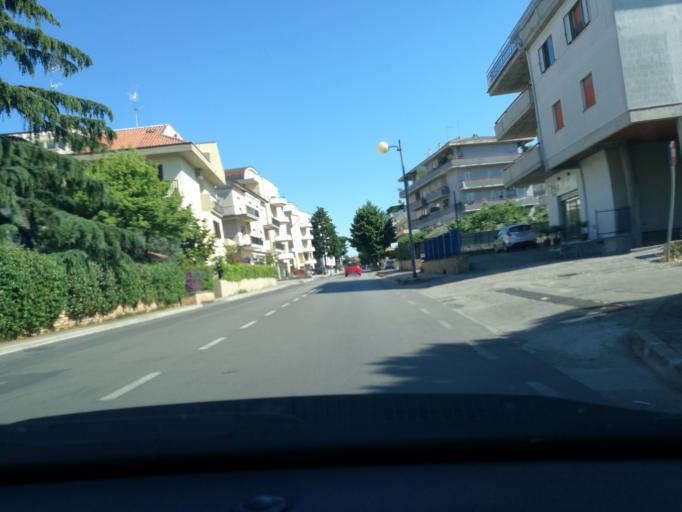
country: IT
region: Abruzzo
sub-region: Provincia di Chieti
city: Vasto
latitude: 42.1273
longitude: 14.7023
